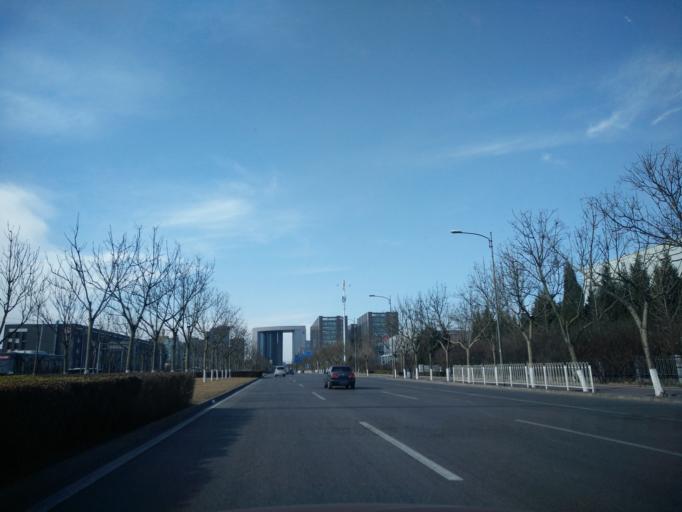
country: CN
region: Beijing
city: Jiugong
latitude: 39.7847
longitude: 116.5245
